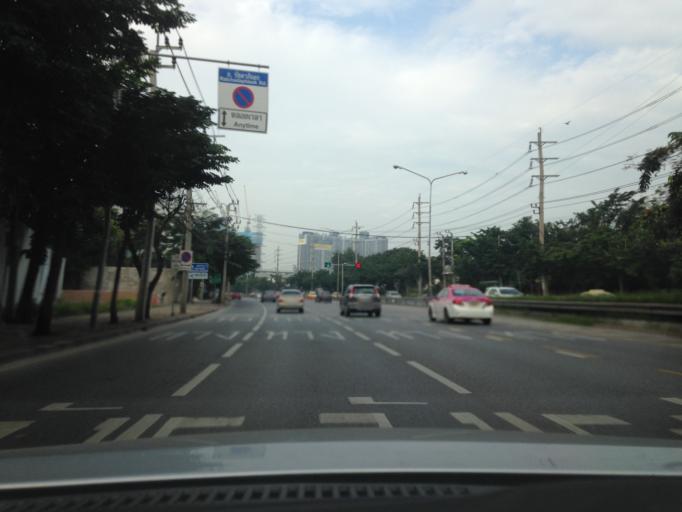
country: TH
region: Bangkok
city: Bang Sue
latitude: 13.8308
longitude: 100.5331
